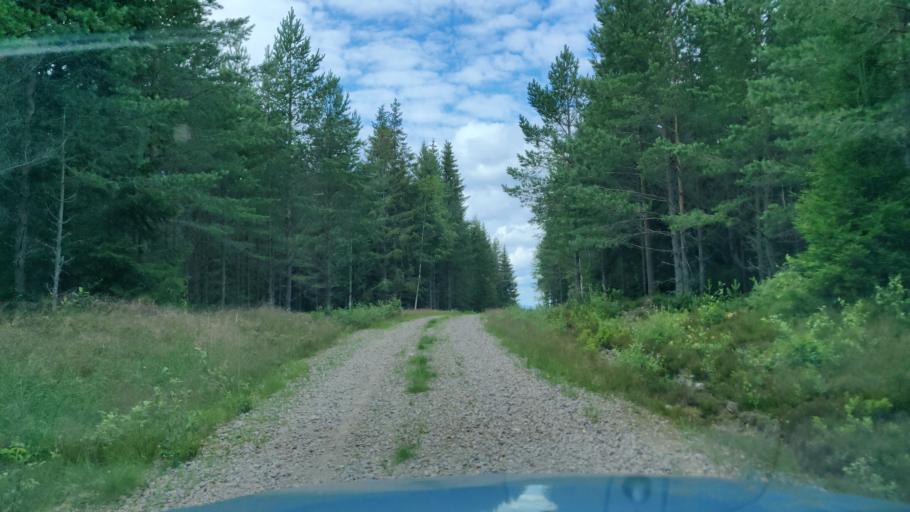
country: SE
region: Vaermland
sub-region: Hagfors Kommun
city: Hagfors
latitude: 59.9658
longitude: 13.5851
